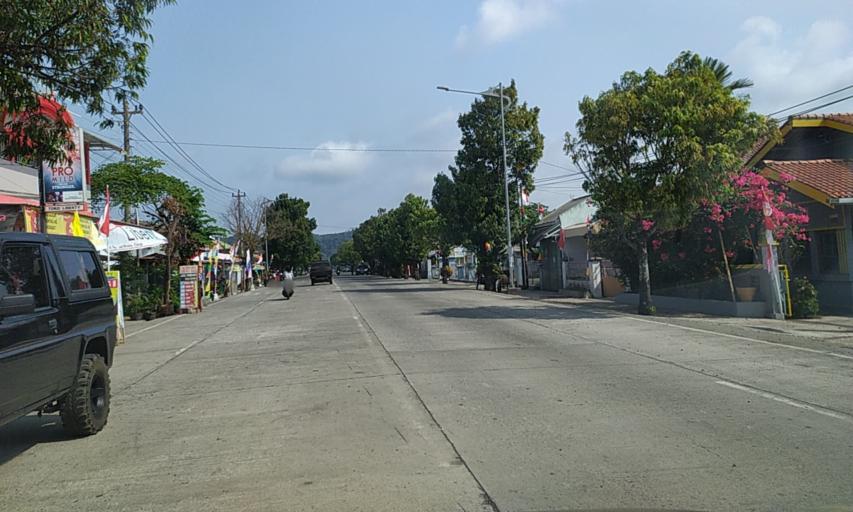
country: ID
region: Central Java
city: Karangbadar Kidul
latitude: -7.7297
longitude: 109.0037
